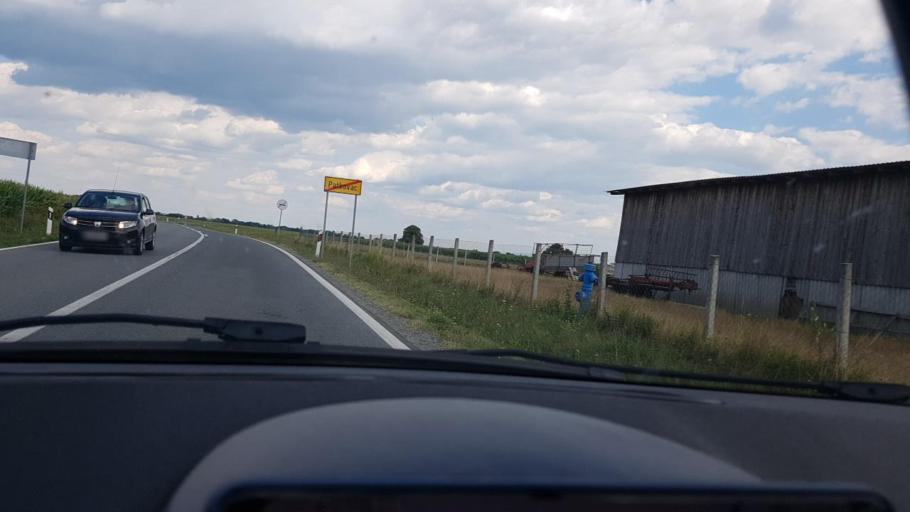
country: HR
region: Bjelovarsko-Bilogorska
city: Zdralovi
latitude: 45.8519
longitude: 16.9335
